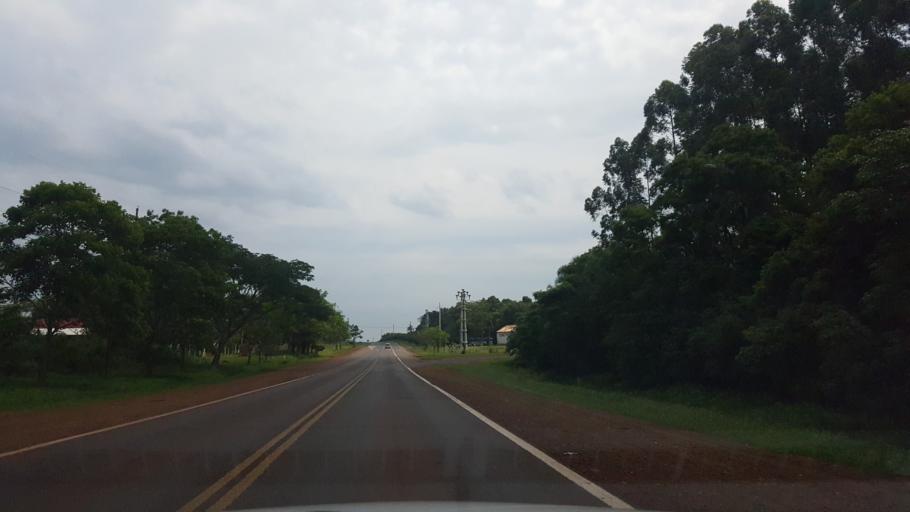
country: AR
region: Misiones
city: Capiovi
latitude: -26.9398
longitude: -55.0782
